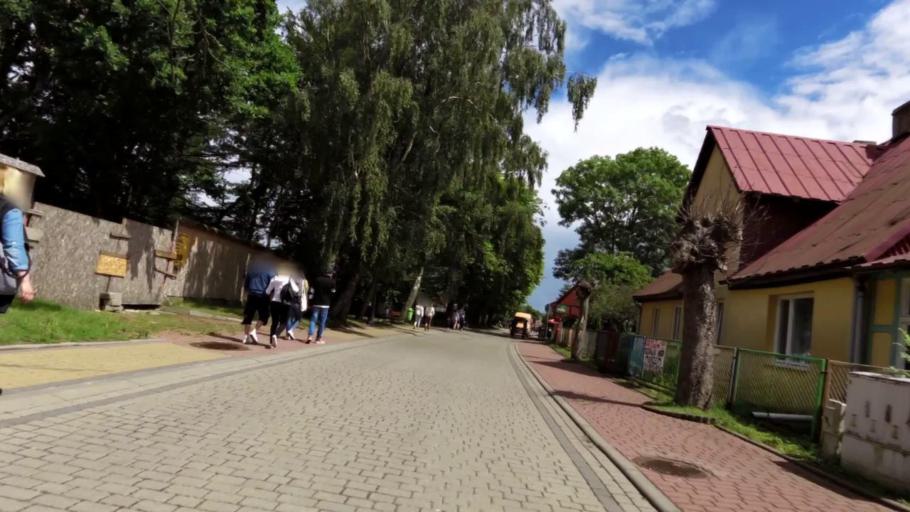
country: PL
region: West Pomeranian Voivodeship
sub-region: Powiat slawienski
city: Darlowo
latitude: 54.5406
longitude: 16.5335
